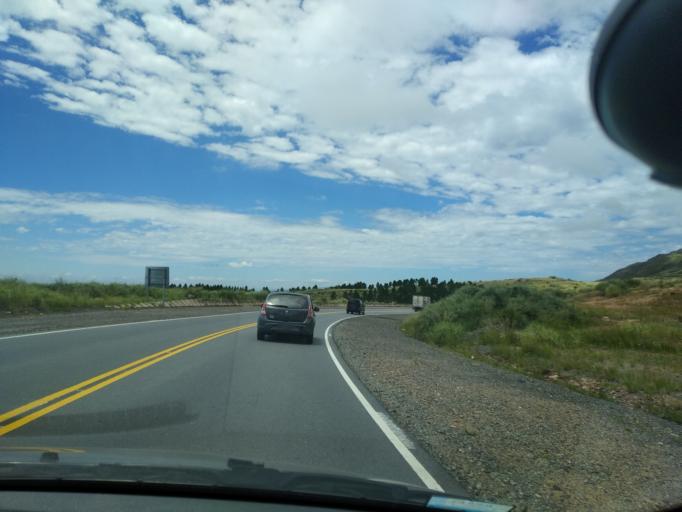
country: AR
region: Cordoba
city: Cuesta Blanca
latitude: -31.6159
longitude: -64.6873
